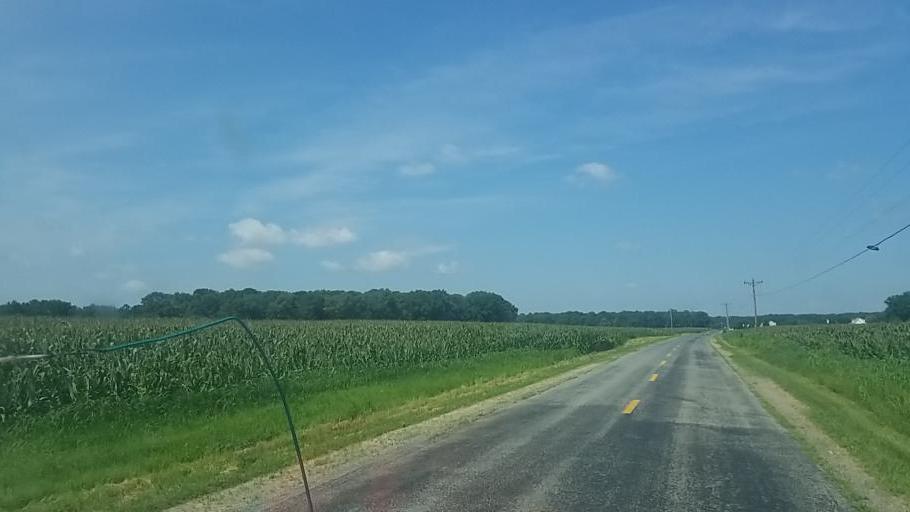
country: US
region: Maryland
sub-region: Caroline County
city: Denton
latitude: 38.8739
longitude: -75.7591
